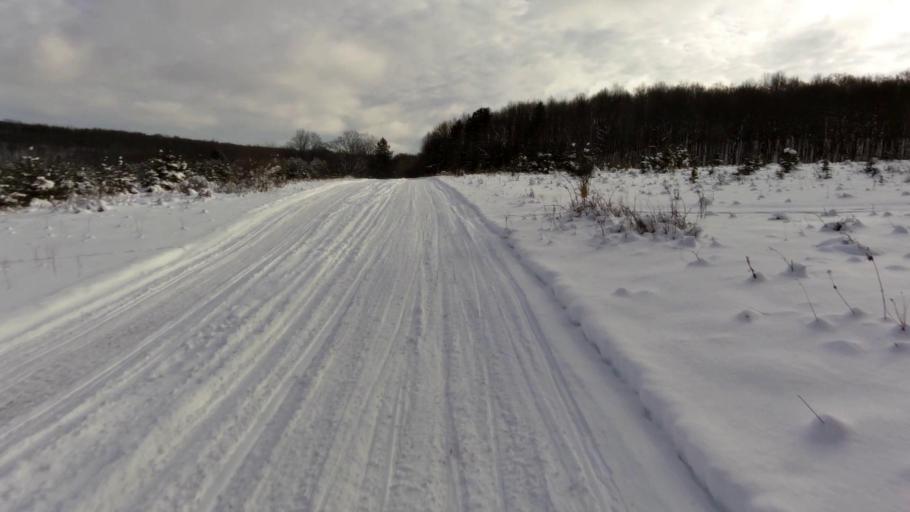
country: US
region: New York
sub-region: Cattaraugus County
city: Franklinville
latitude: 42.3117
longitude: -78.5340
